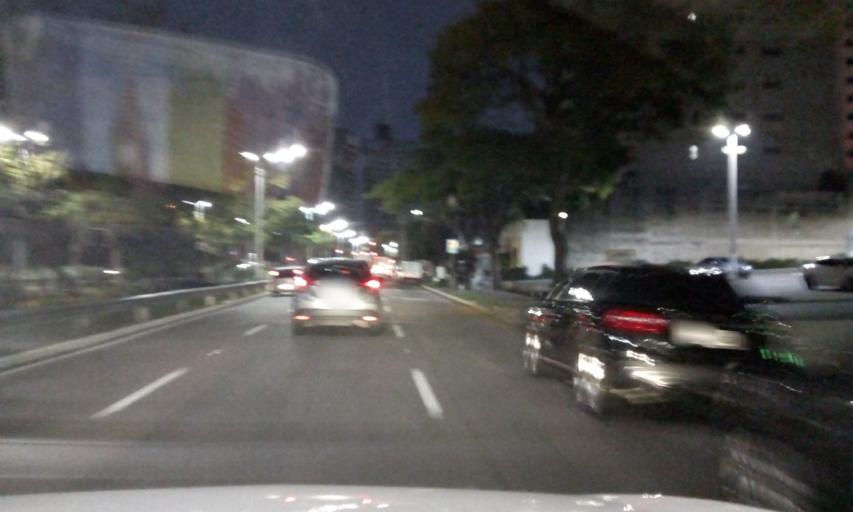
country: BR
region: Sao Paulo
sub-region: Jundiai
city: Jundiai
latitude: -23.1877
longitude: -46.8915
